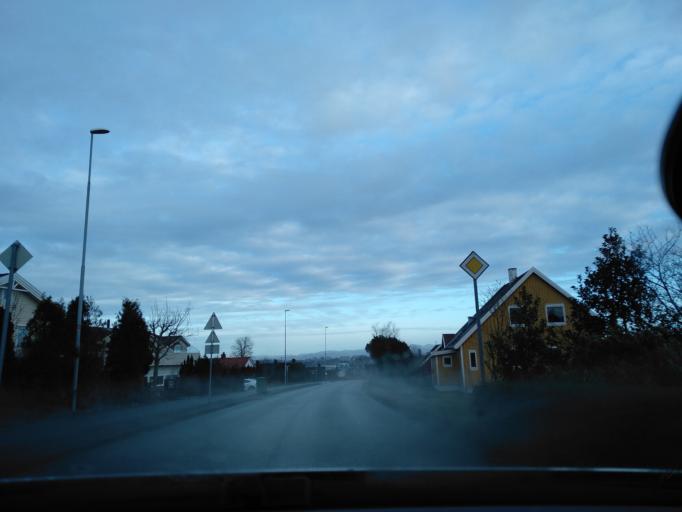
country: NO
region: Rogaland
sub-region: Sola
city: Sola
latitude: 58.9404
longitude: 5.6494
